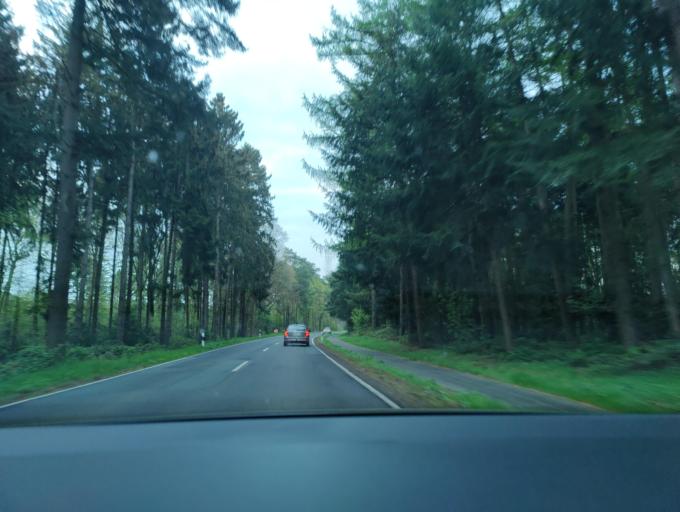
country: DE
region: Lower Saxony
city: Lingen
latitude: 52.4808
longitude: 7.2482
